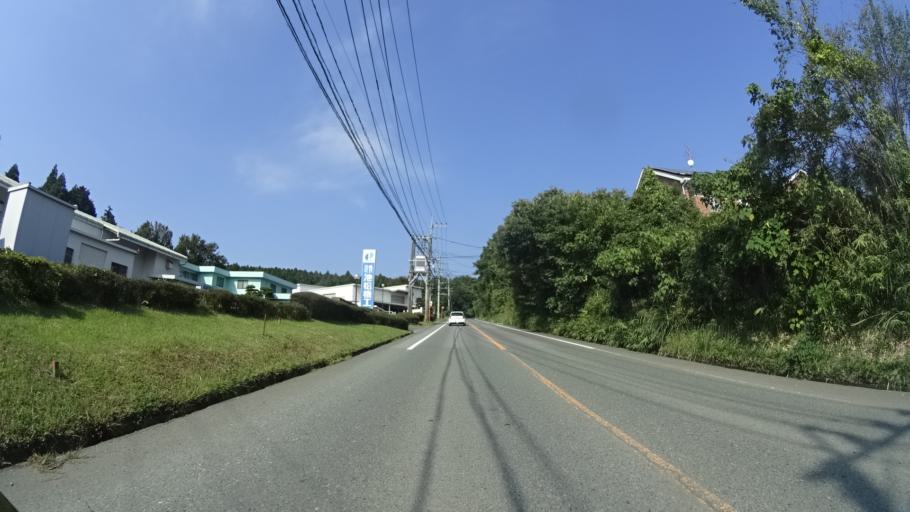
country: JP
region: Kumamoto
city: Ozu
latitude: 32.8835
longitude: 130.8939
